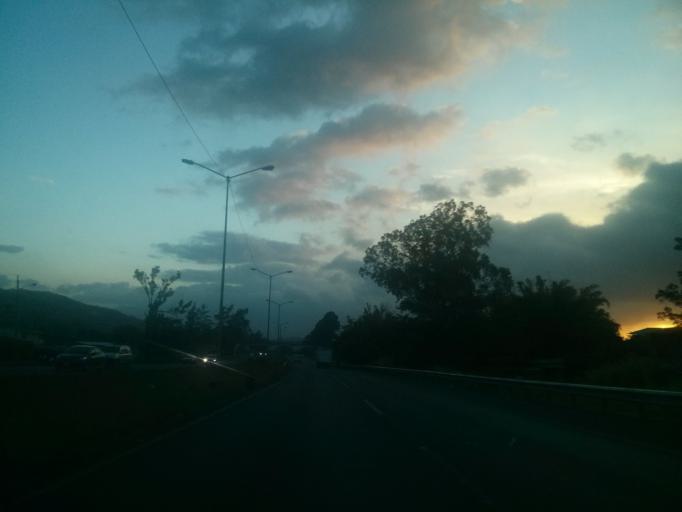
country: CR
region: Cartago
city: Tres Rios
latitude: 9.9041
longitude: -83.9822
